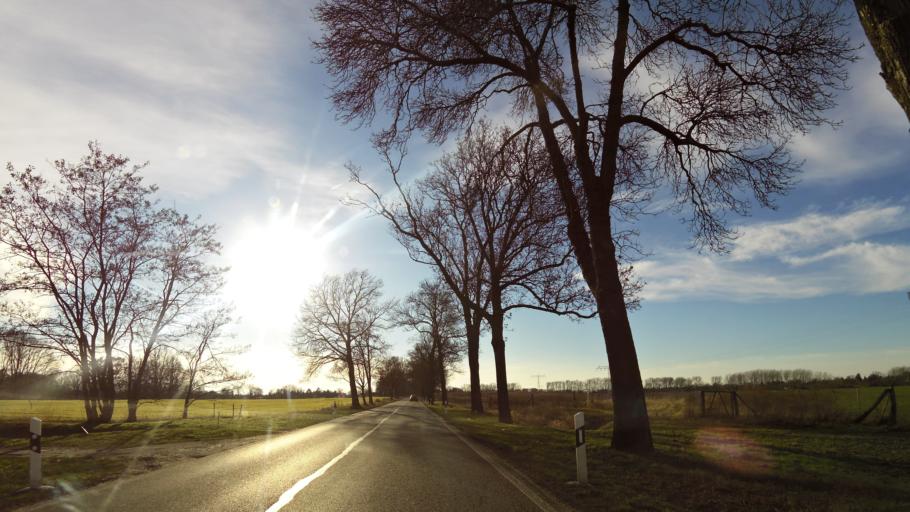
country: DE
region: Brandenburg
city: Neuenhagen
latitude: 52.5059
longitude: 13.7301
